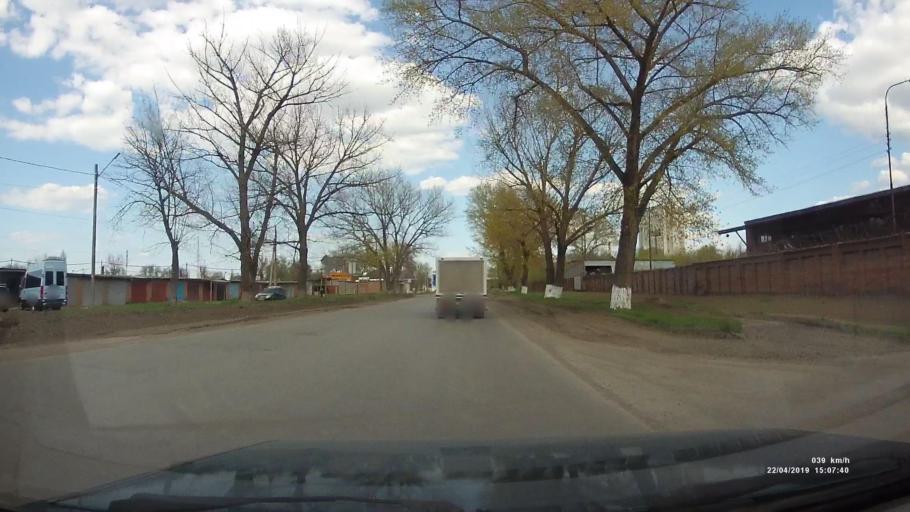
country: RU
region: Rostov
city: Azov
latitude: 47.0961
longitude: 39.4053
